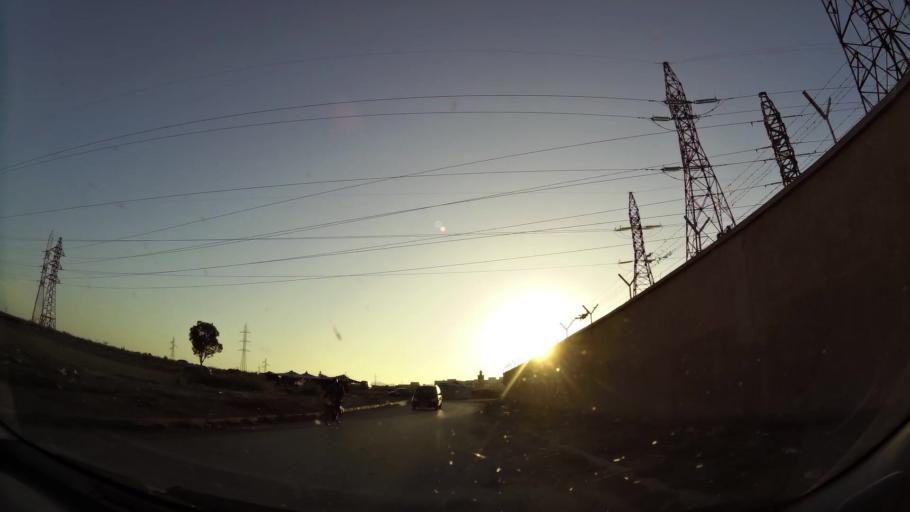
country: MA
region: Oriental
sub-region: Oujda-Angad
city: Oujda
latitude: 34.7111
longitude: -1.9156
